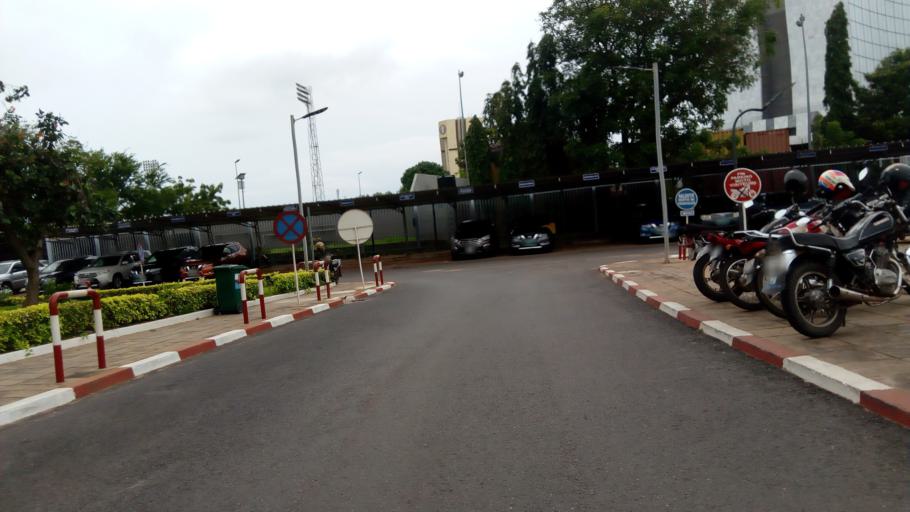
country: TG
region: Maritime
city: Lome
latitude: 6.1284
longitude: 1.2165
